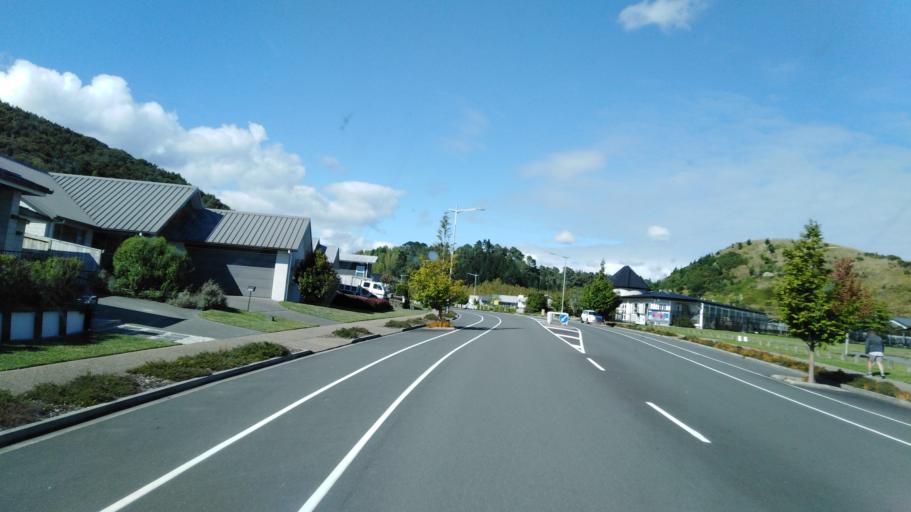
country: NZ
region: Bay of Plenty
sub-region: Tauranga City
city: Tauranga
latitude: -37.7557
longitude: 176.1041
